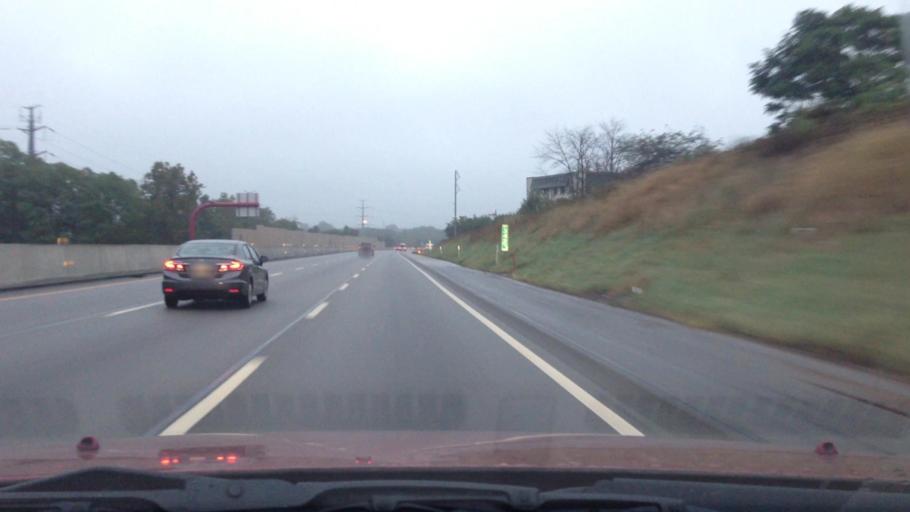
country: US
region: Pennsylvania
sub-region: Montgomery County
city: Horsham
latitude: 40.1580
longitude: -75.1316
